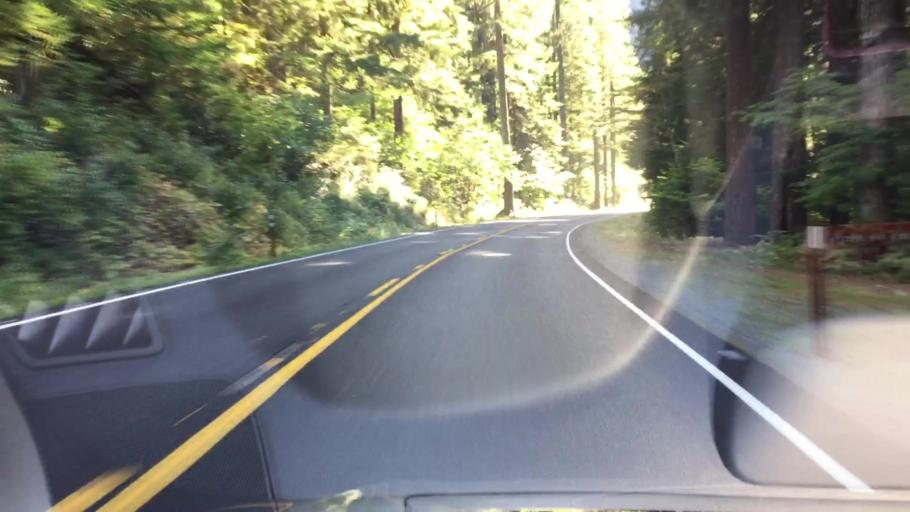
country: US
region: Washington
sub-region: Pierce County
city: Buckley
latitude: 46.7091
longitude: -121.5769
